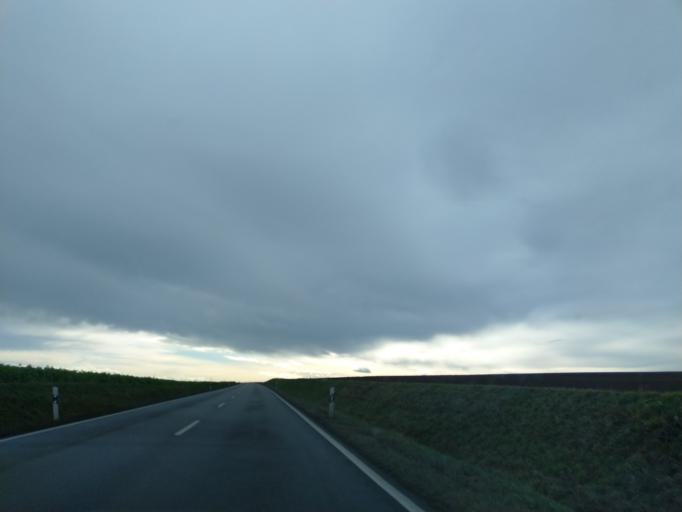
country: DE
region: Bavaria
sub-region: Lower Bavaria
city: Osterhofen
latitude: 48.6774
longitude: 13.0319
